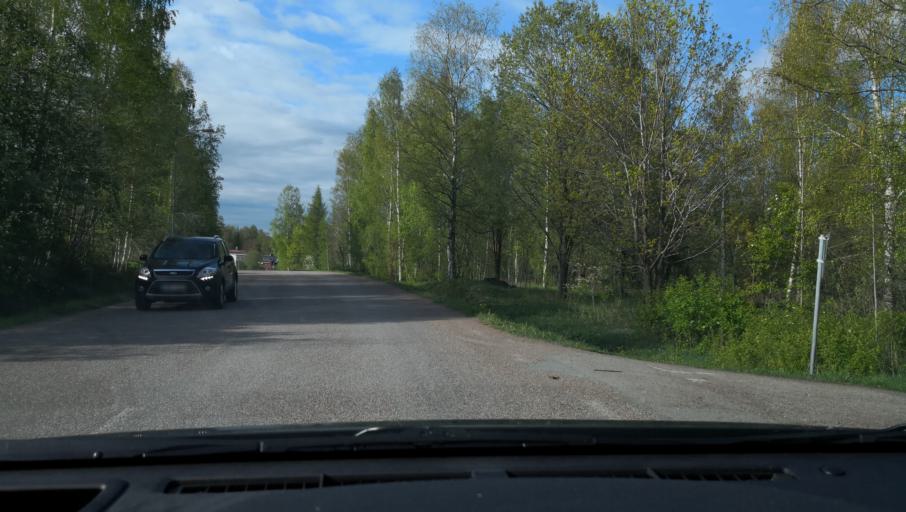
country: SE
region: Dalarna
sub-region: Saters Kommun
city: Saeter
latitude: 60.2947
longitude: 15.8267
